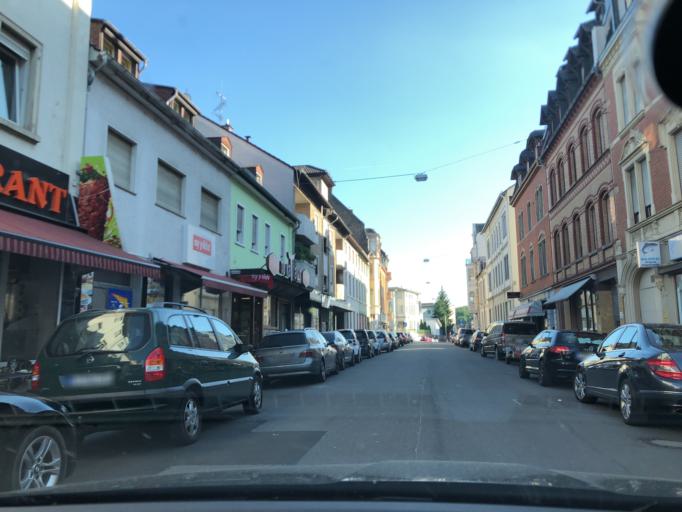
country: DE
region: Hesse
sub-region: Regierungsbezirk Darmstadt
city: Wiesbaden
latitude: 50.0384
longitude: 8.2381
